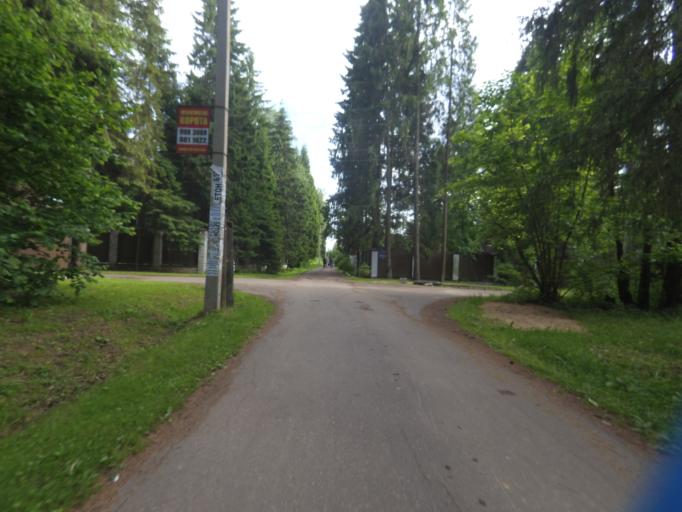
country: RU
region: Moskovskaya
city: Nekrasovskiy
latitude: 56.1119
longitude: 37.5170
